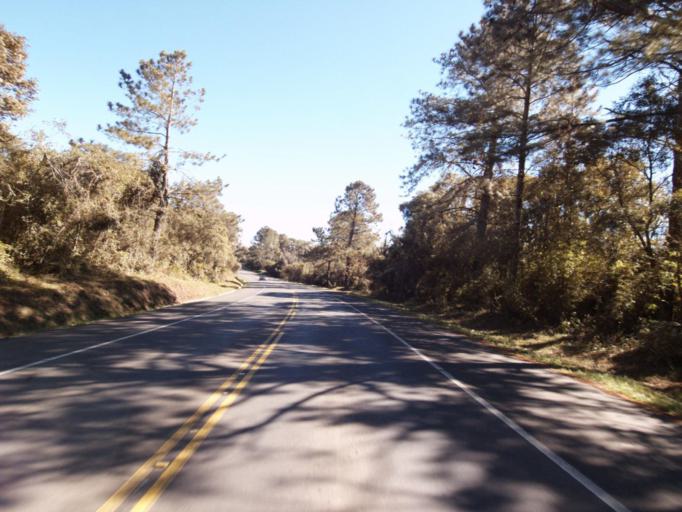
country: BR
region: Santa Catarina
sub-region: Joacaba
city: Joacaba
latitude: -27.1096
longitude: -51.6339
